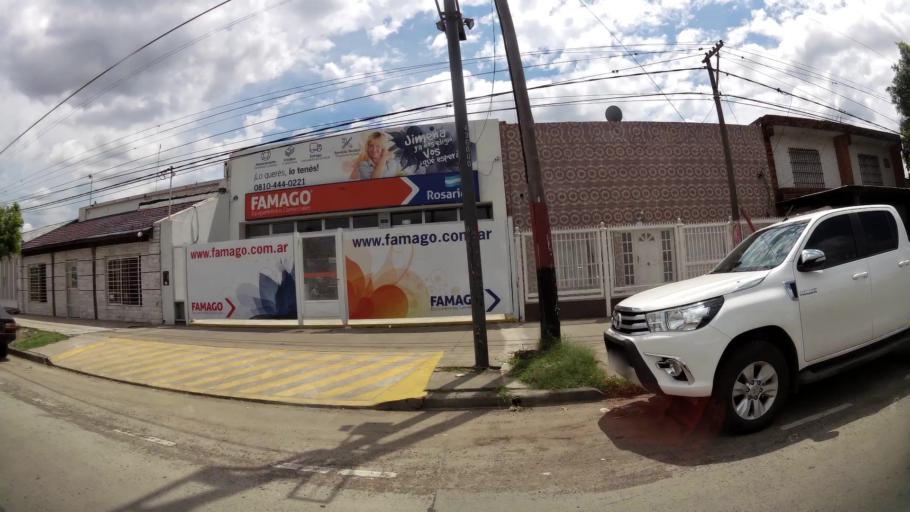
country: AR
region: Santa Fe
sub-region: Departamento de Rosario
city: Rosario
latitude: -32.9851
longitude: -60.6638
